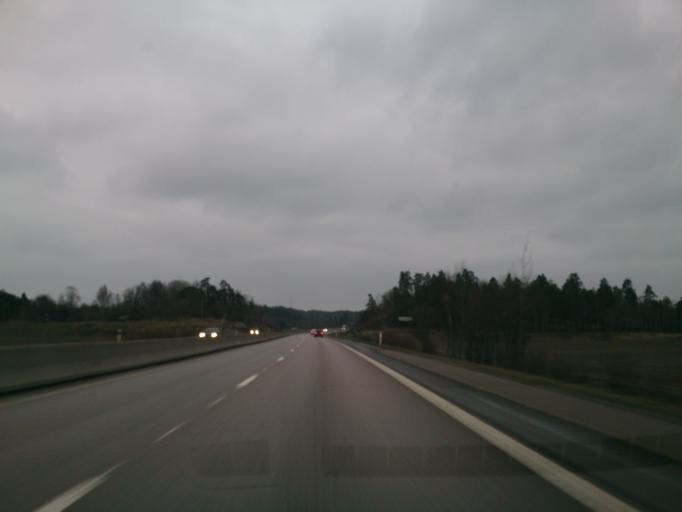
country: SE
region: OEstergoetland
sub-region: Norrkopings Kommun
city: Kimstad
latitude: 58.5586
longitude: 16.0601
